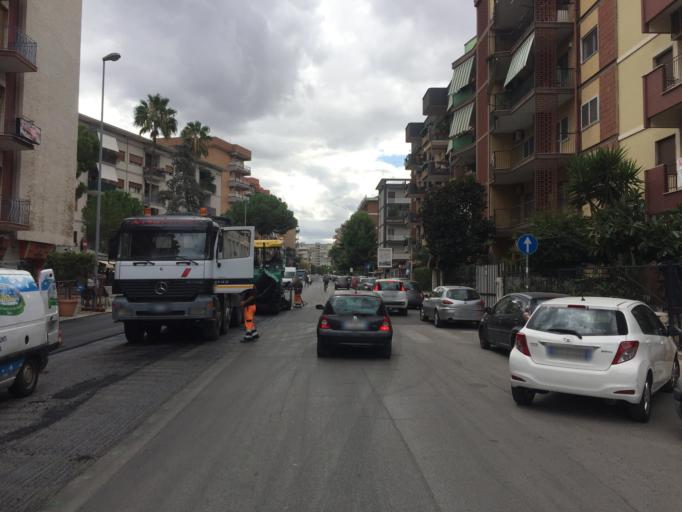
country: IT
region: Apulia
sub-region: Provincia di Bari
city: Bari
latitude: 41.1044
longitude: 16.8596
